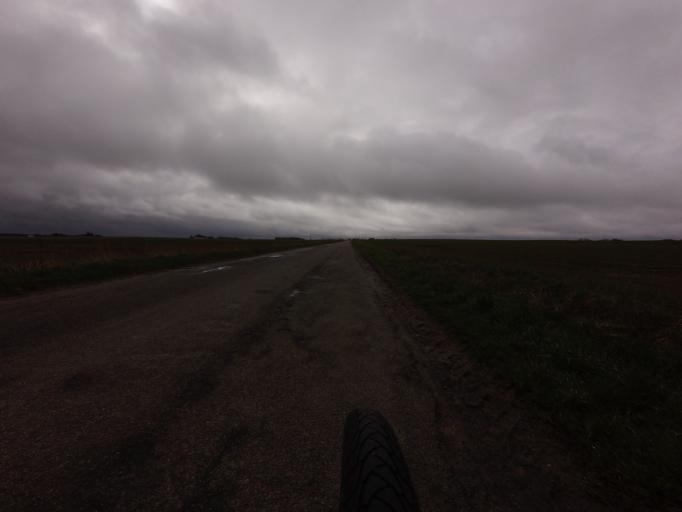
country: DK
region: North Denmark
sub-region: Hjorring Kommune
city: Vra
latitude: 57.3783
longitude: 9.8388
